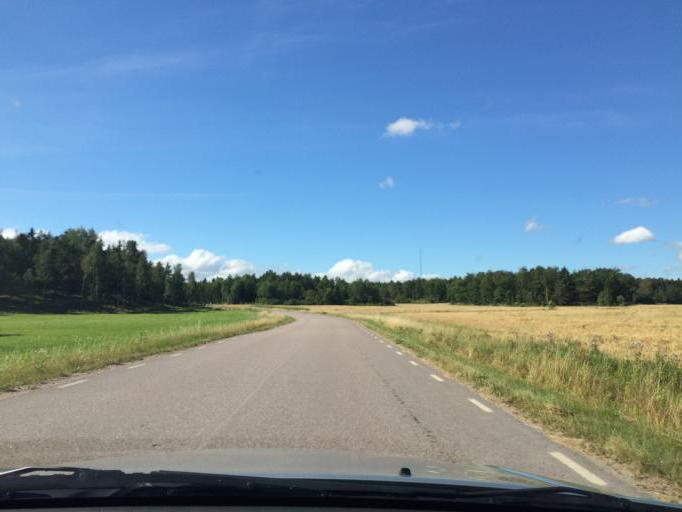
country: SE
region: Soedermanland
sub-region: Eskilstuna Kommun
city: Torshalla
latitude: 59.5236
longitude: 16.4404
